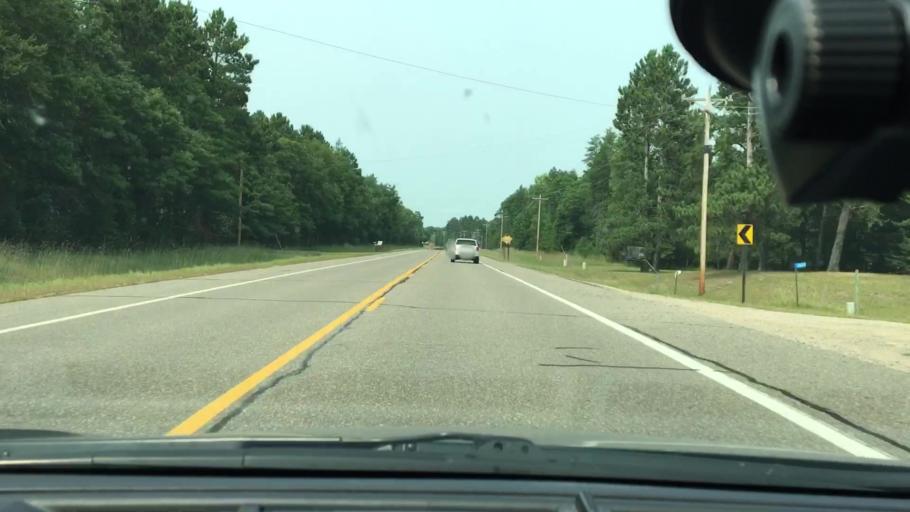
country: US
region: Minnesota
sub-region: Crow Wing County
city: Cross Lake
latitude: 46.5686
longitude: -94.1287
